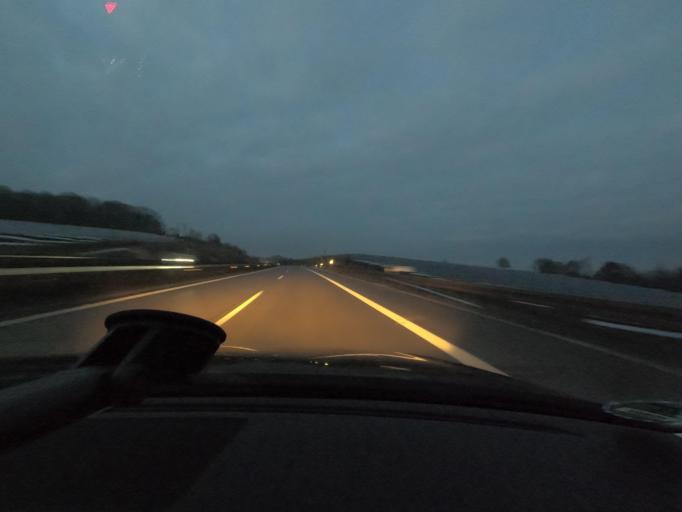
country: DE
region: Thuringia
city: Bockstadt
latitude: 50.3742
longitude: 10.9200
